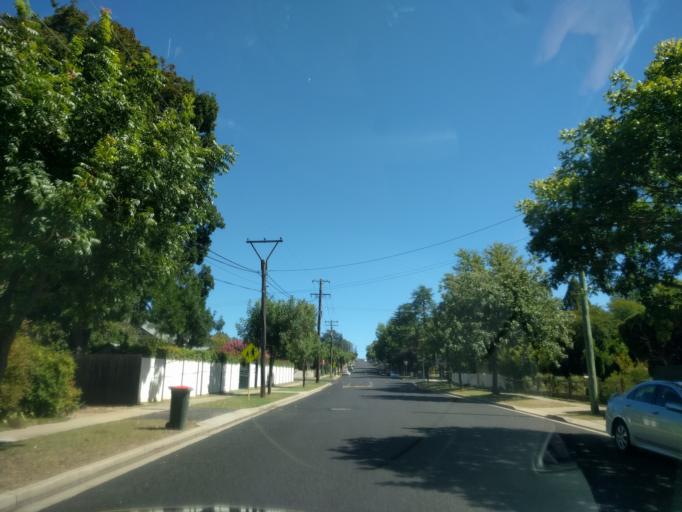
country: AU
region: New South Wales
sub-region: Armidale Dumaresq
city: Armidale
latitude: -30.5181
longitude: 151.6656
